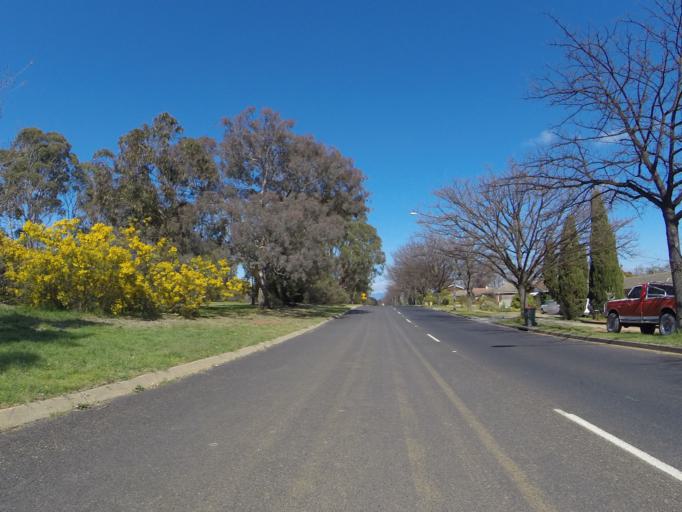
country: AU
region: Australian Capital Territory
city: Canberra
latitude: -35.2400
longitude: 149.1648
